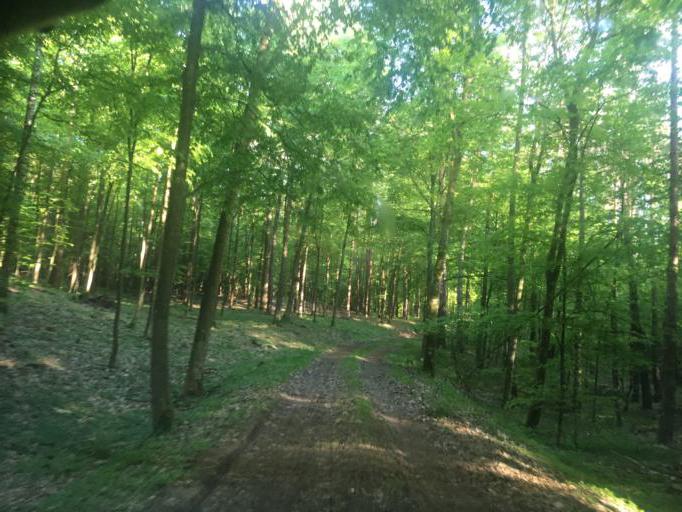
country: PL
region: Kujawsko-Pomorskie
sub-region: Powiat brodnicki
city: Gorzno
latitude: 53.2116
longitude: 19.7206
